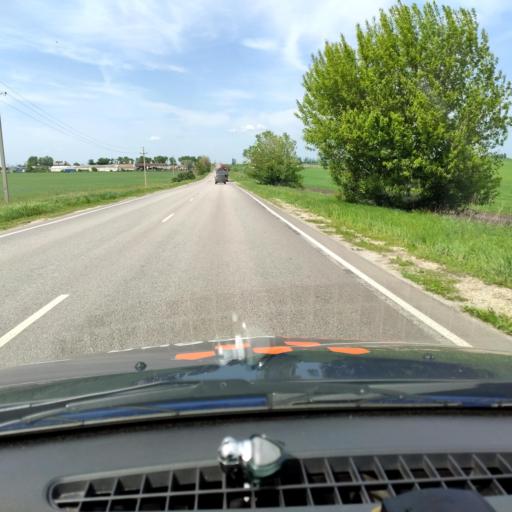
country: RU
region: Voronezj
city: Novaya Usman'
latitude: 51.5741
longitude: 39.3752
